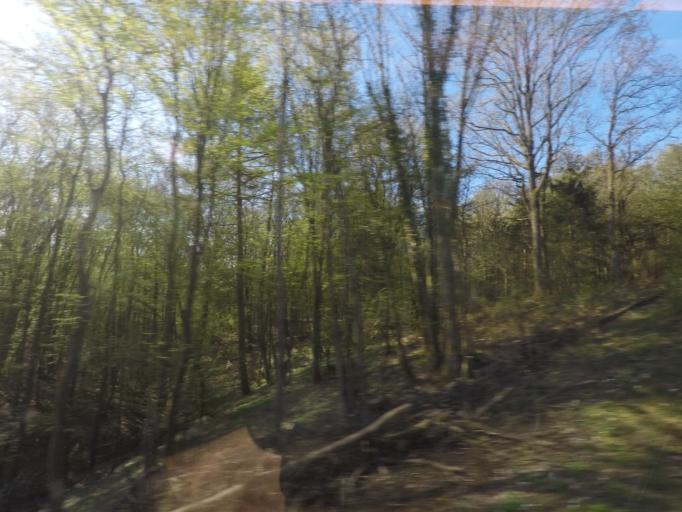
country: BE
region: Wallonia
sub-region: Province de Namur
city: Rochefort
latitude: 50.2487
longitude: 5.2527
